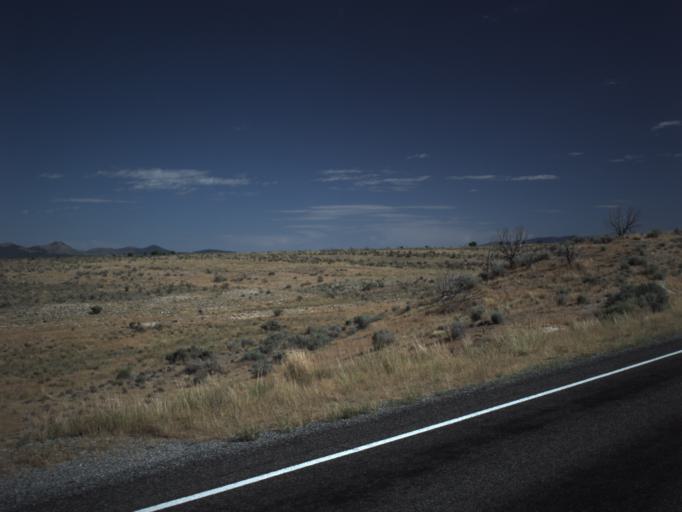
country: US
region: Utah
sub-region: Juab County
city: Mona
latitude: 39.7401
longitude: -112.1890
